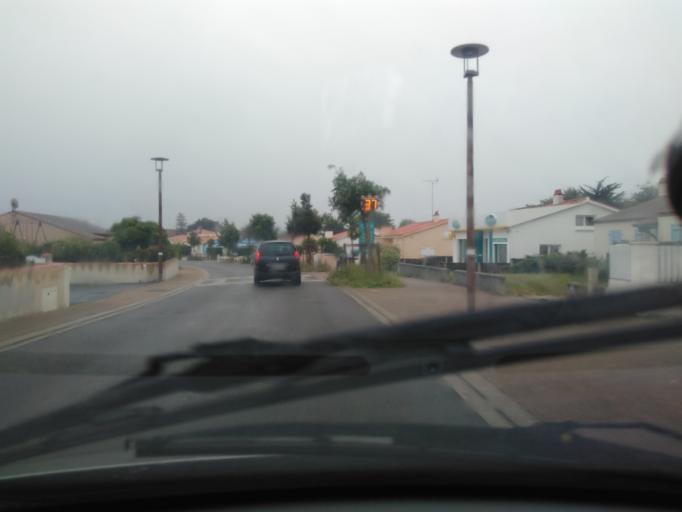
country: FR
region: Pays de la Loire
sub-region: Departement de la Vendee
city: Bretignolles-sur-Mer
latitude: 46.6311
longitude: -1.8599
